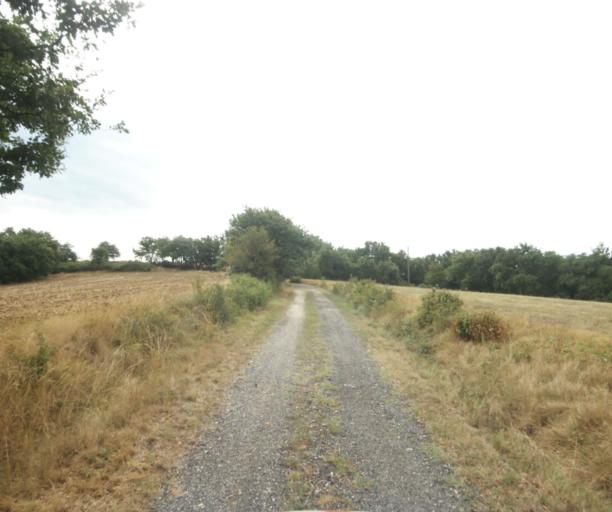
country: FR
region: Midi-Pyrenees
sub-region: Departement de la Haute-Garonne
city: Revel
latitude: 43.4400
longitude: 1.9737
